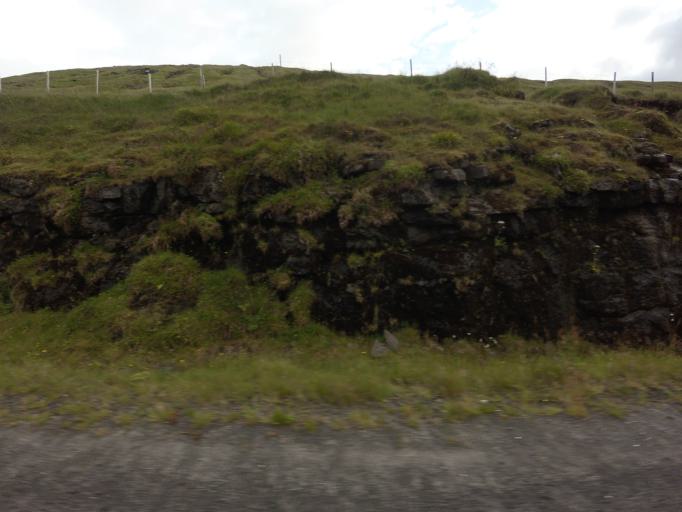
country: FO
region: Streymoy
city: Kollafjordhur
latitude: 62.1662
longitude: -6.9550
